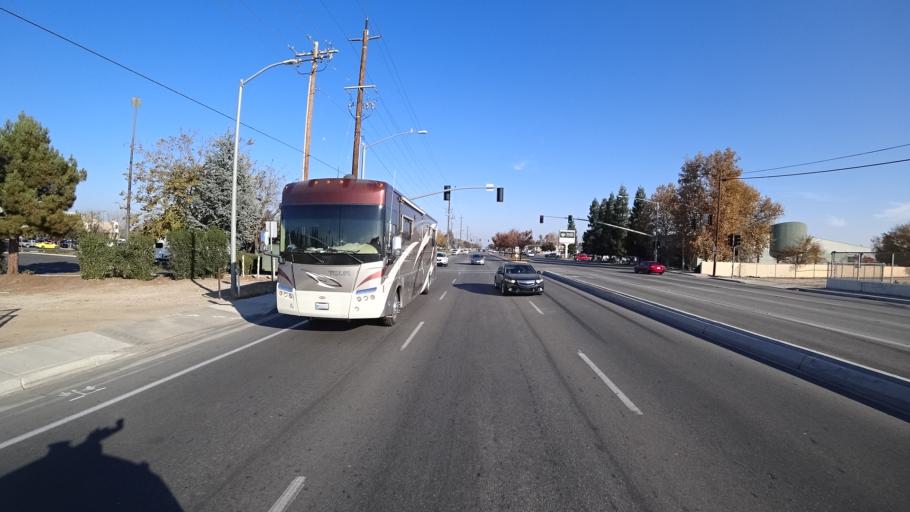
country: US
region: California
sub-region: Kern County
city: Greenfield
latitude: 35.2959
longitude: -119.0590
